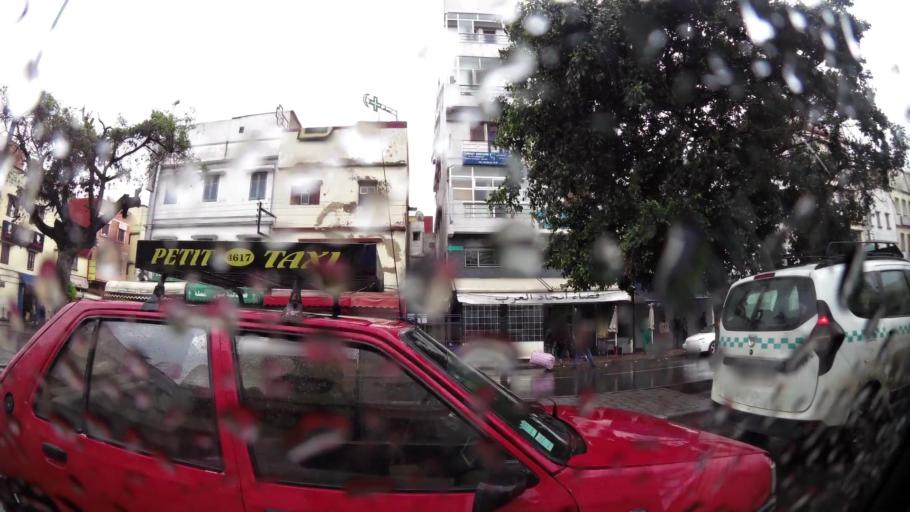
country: MA
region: Grand Casablanca
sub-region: Casablanca
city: Casablanca
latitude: 33.5489
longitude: -7.5720
